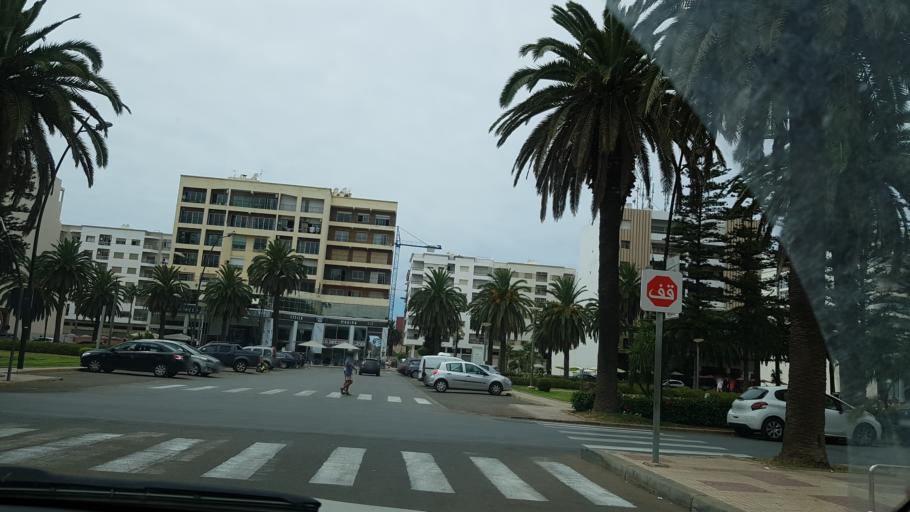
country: MA
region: Grand Casablanca
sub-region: Mohammedia
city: Mohammedia
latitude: 33.7048
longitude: -7.3978
